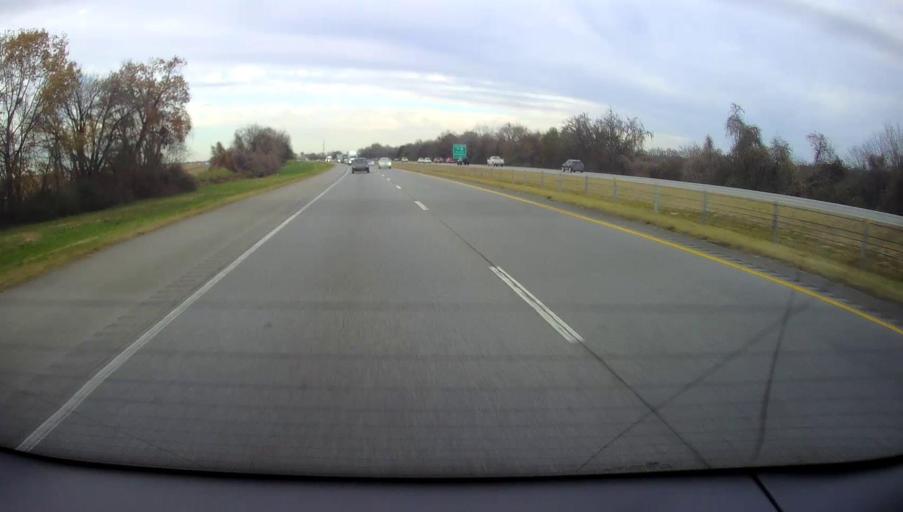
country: US
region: Alabama
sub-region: Morgan County
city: Priceville
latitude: 34.6051
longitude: -86.8985
